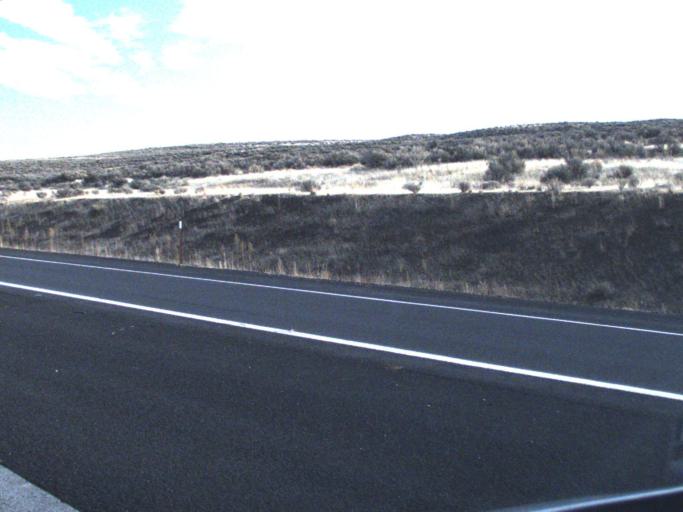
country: US
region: Washington
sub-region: Adams County
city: Ritzville
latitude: 46.9746
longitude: -118.5662
